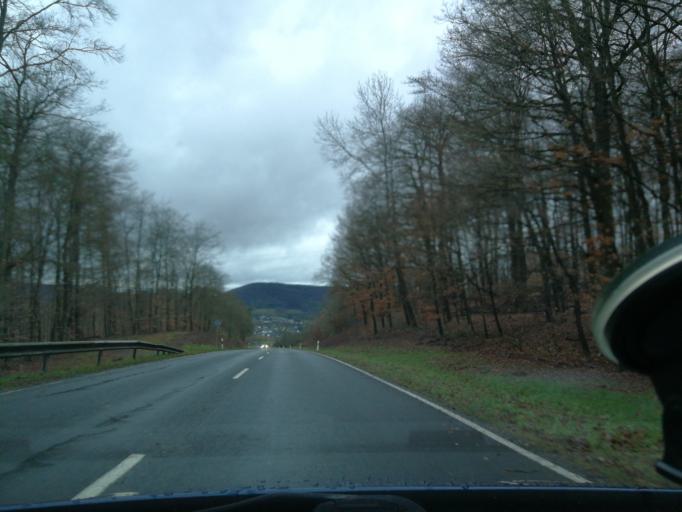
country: DE
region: Rheinland-Pfalz
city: Salmtal
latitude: 49.9182
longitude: 6.8676
